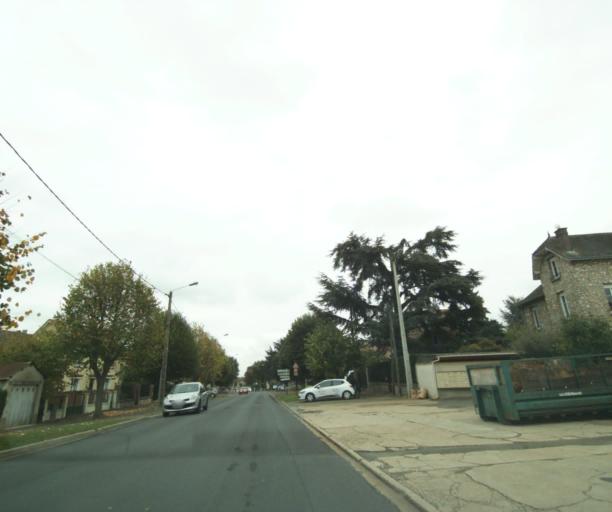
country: FR
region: Centre
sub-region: Departement d'Eure-et-Loir
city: Dreux
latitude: 48.7400
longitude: 1.3513
